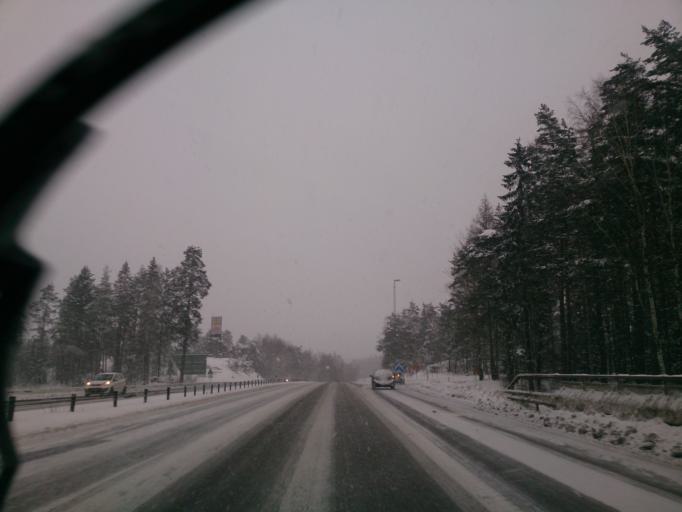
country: SE
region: Soedermanland
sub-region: Nykopings Kommun
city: Nykoping
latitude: 58.7637
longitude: 16.9908
